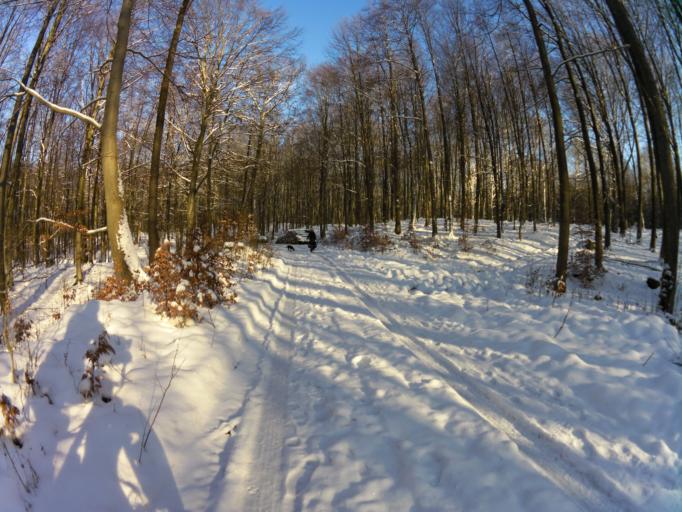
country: PL
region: West Pomeranian Voivodeship
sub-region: Powiat stargardzki
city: Insko
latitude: 53.3887
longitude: 15.5426
